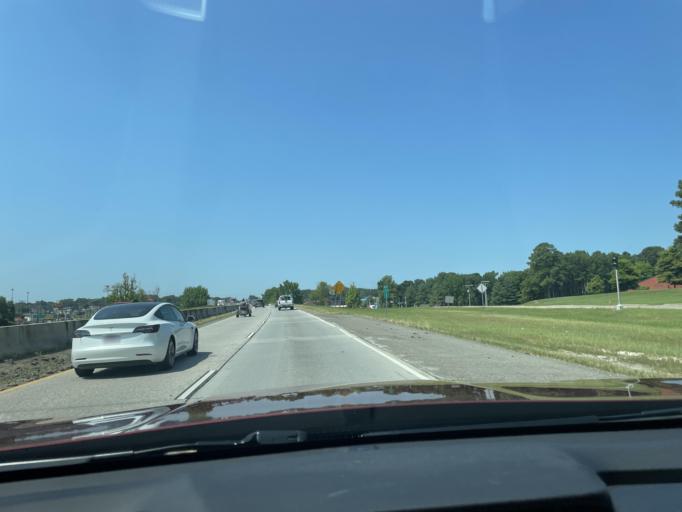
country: US
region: Arkansas
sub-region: Pulaski County
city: Jacksonville
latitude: 34.8890
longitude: -92.1052
